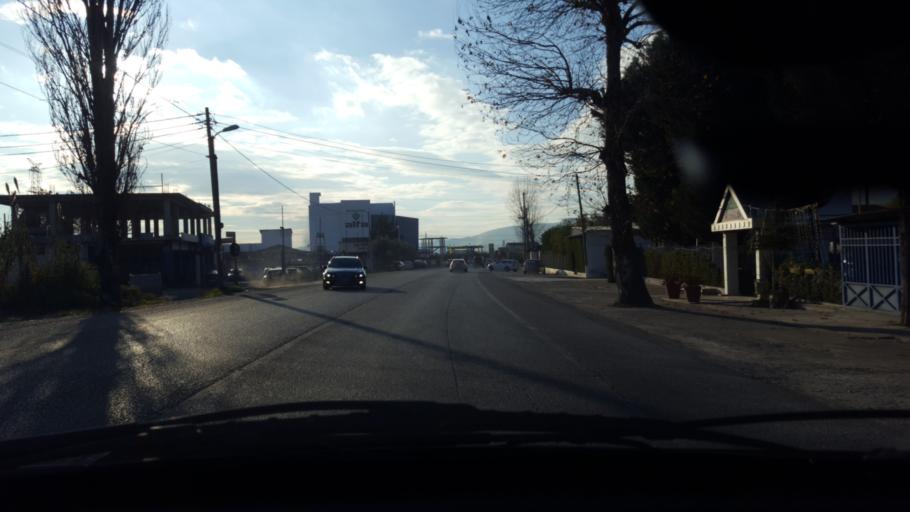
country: AL
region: Elbasan
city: Elbasan
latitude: 41.1013
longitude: 20.0549
